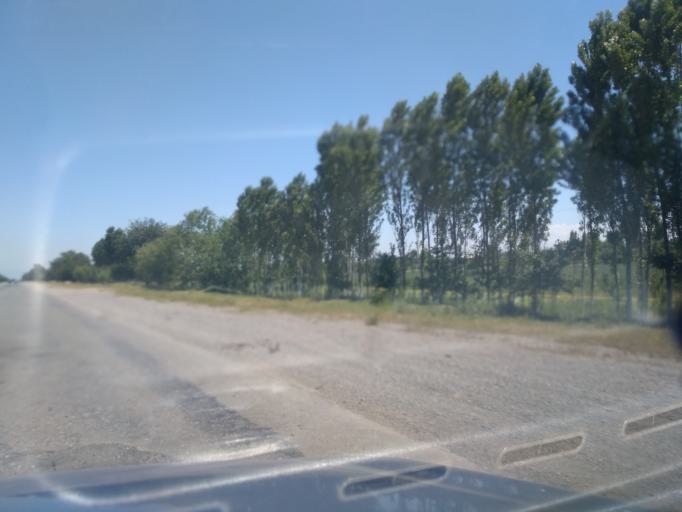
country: TJ
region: Viloyati Sughd
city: Zafarobod
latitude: 40.2228
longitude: 68.9334
